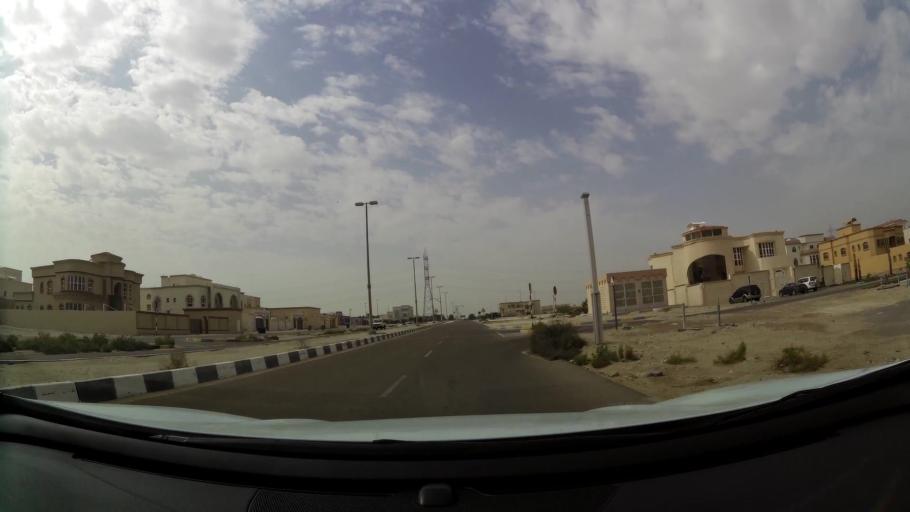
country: AE
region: Abu Dhabi
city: Abu Dhabi
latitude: 24.3088
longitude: 54.6485
